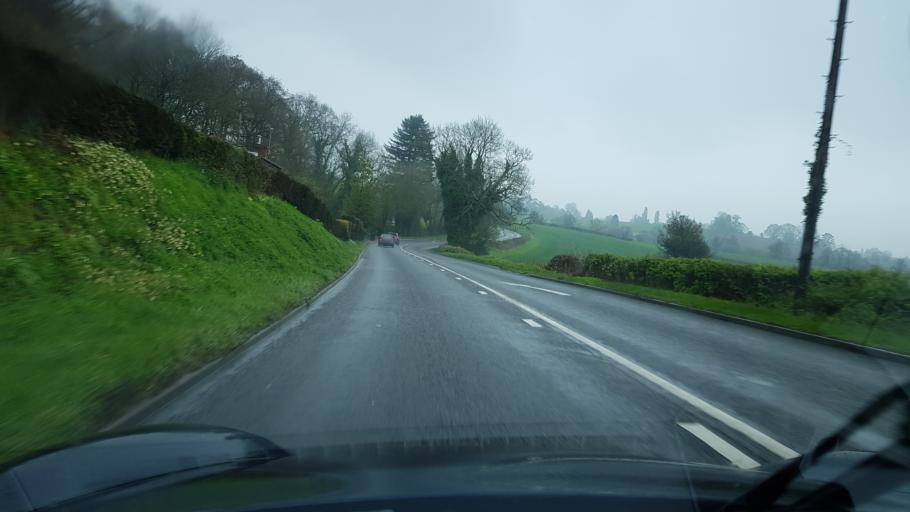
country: GB
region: England
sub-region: Gloucestershire
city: Newent
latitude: 51.8654
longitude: -2.4189
